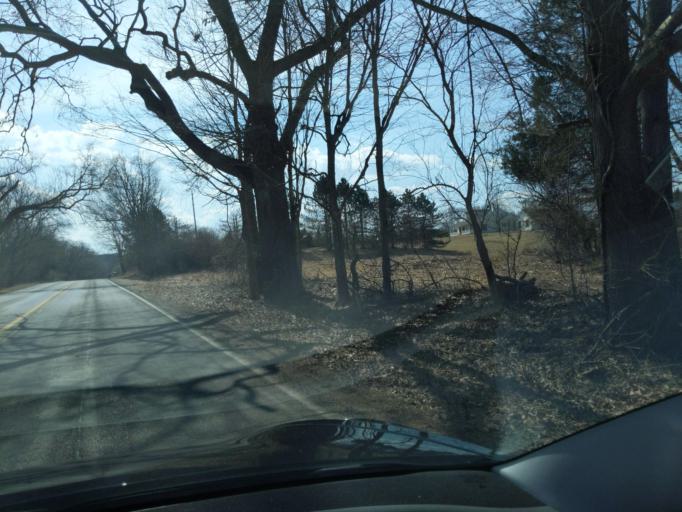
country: US
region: Michigan
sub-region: Washtenaw County
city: Chelsea
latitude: 42.4207
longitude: -84.0535
